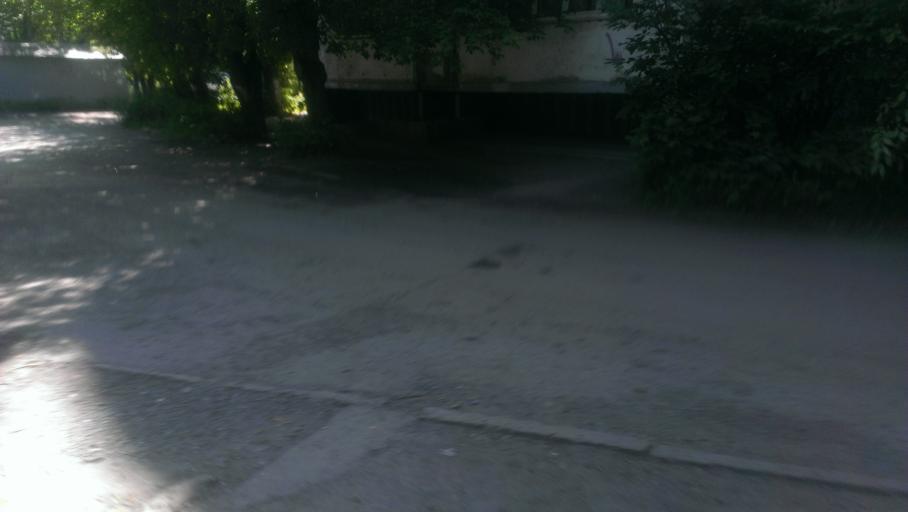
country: RU
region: Altai Krai
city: Novosilikatnyy
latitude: 53.3465
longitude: 83.6822
